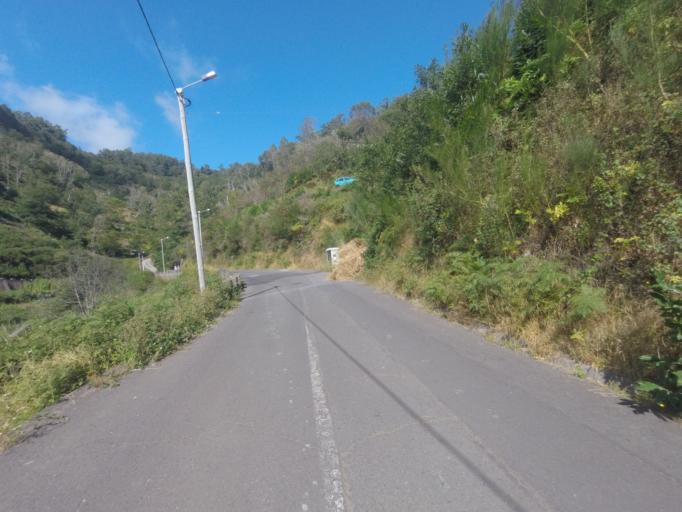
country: PT
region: Madeira
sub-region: Ribeira Brava
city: Campanario
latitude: 32.7021
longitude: -17.0157
